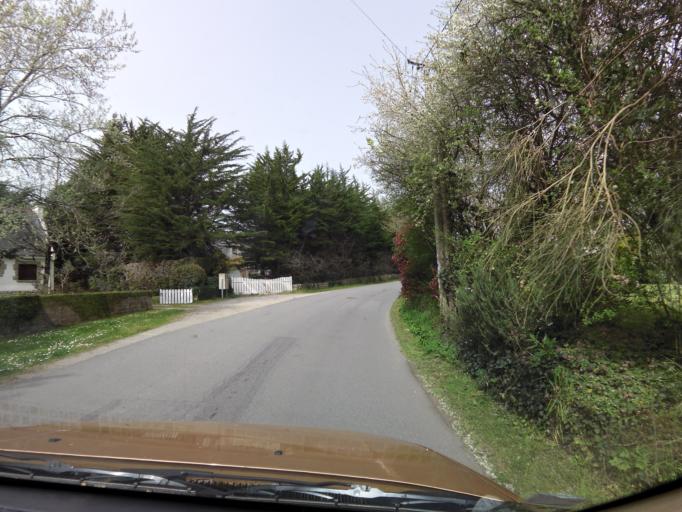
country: FR
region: Brittany
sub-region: Departement du Morbihan
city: Sene
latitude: 47.5786
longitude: -2.7132
